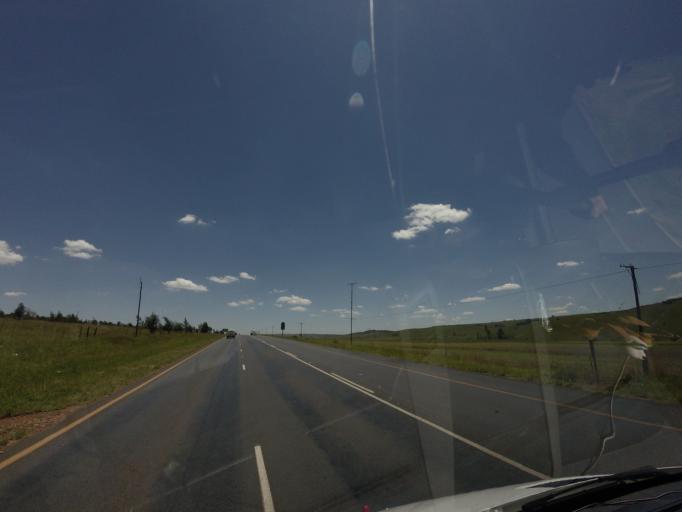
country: ZA
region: Mpumalanga
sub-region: Nkangala District Municipality
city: Belfast
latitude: -25.6759
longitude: 30.2306
